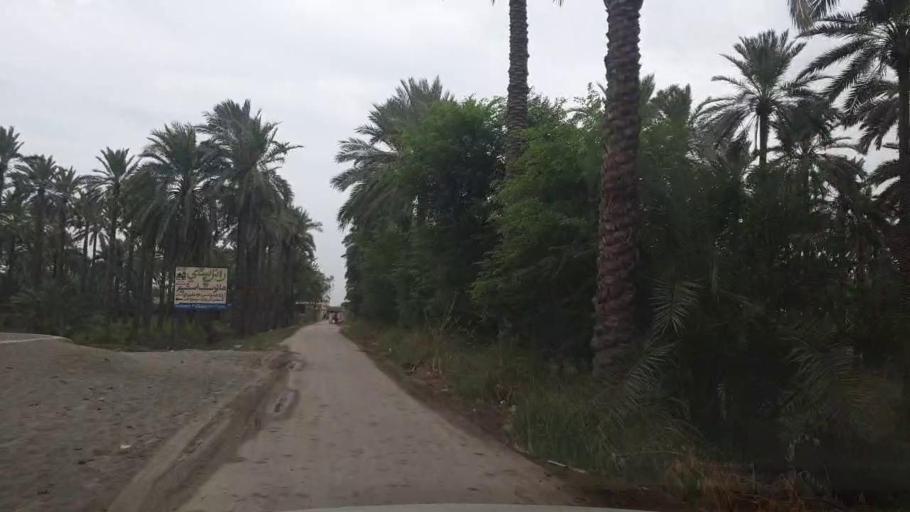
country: PK
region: Sindh
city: Khairpur
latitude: 27.5538
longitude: 68.7507
